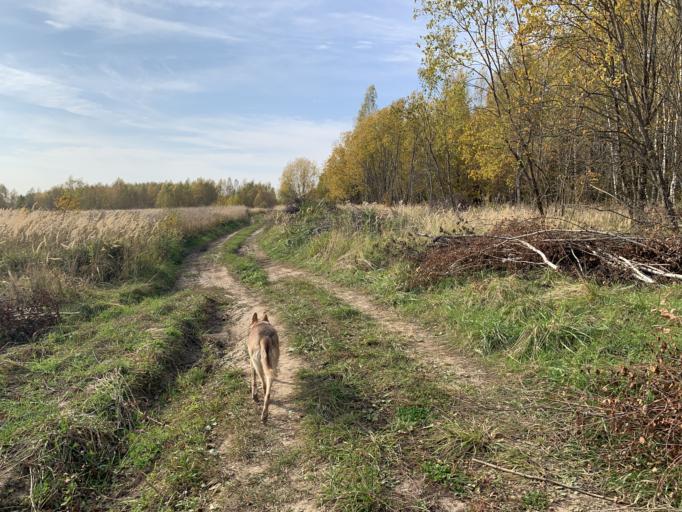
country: RU
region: Jaroslavl
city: Porech'ye-Rybnoye
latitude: 56.9880
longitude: 39.3967
